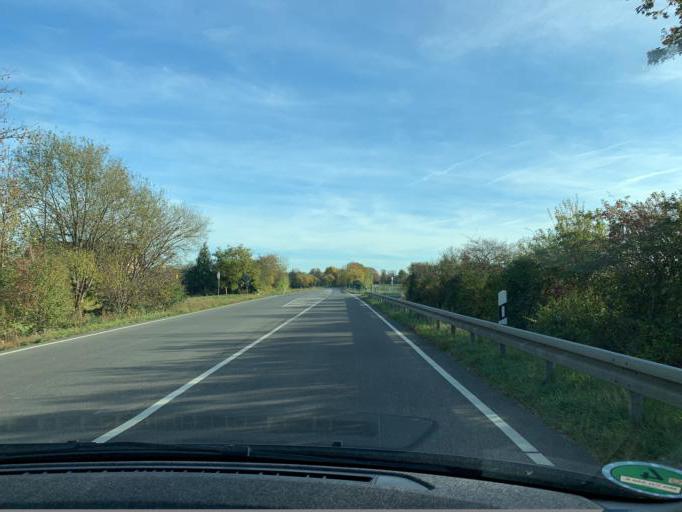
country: DE
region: North Rhine-Westphalia
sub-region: Regierungsbezirk Koln
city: Kreuzau
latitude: 50.7330
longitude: 6.5058
